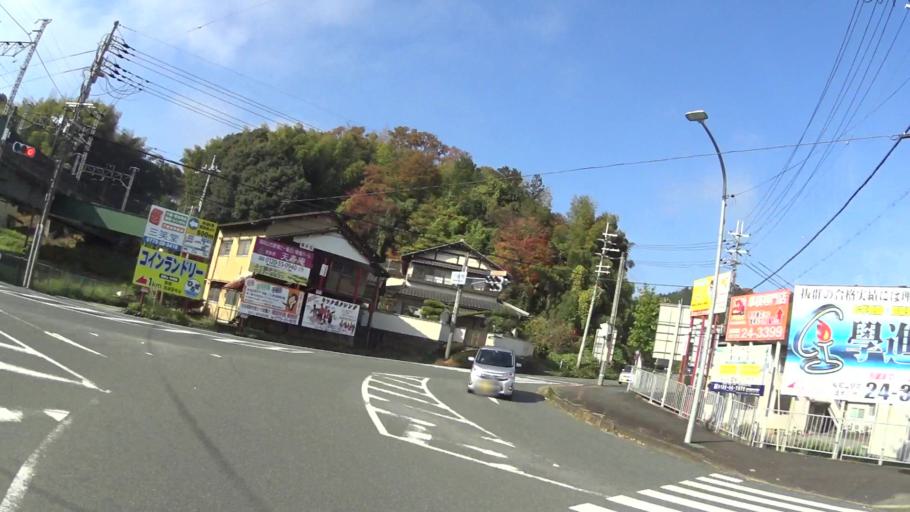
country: JP
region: Kyoto
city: Fukuchiyama
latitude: 35.3018
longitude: 135.1088
